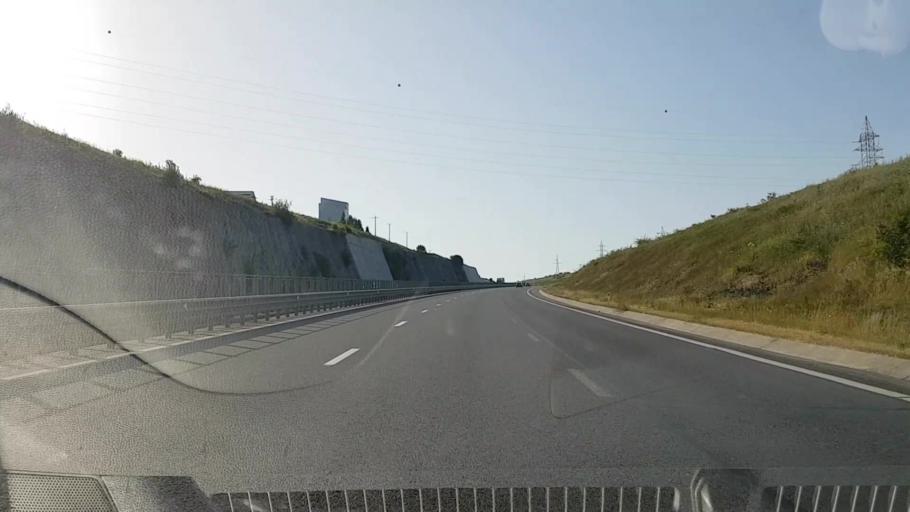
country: RO
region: Cluj
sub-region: Comuna Sandulesti
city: Sandulesti
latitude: 46.5949
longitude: 23.7131
